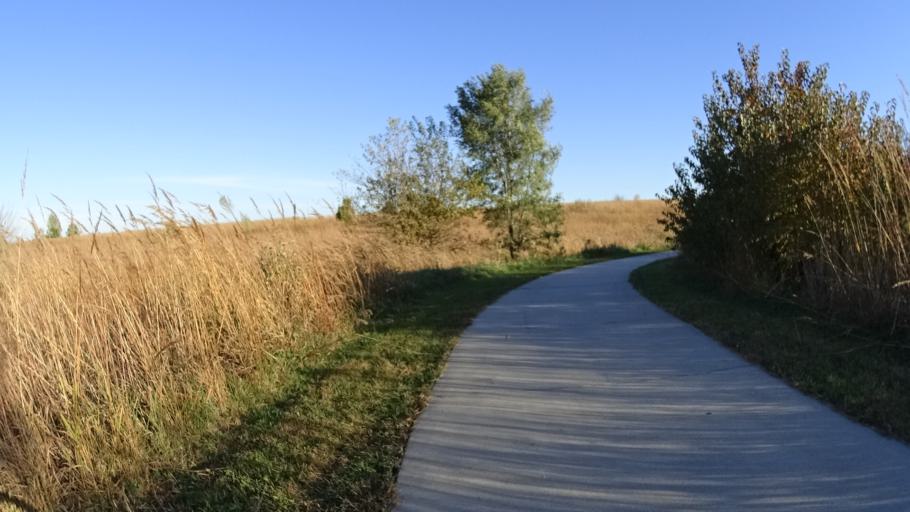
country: US
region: Nebraska
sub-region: Sarpy County
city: Papillion
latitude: 41.1426
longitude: -96.0748
